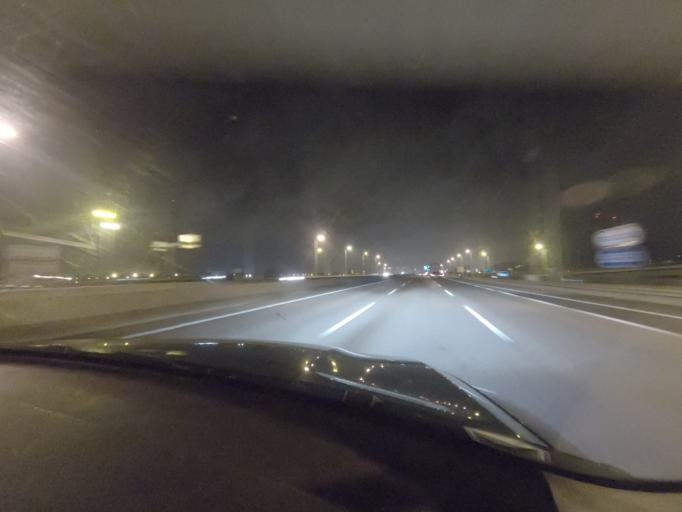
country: PT
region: Lisbon
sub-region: Alenquer
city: Carregado
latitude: 39.0155
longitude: -8.9663
